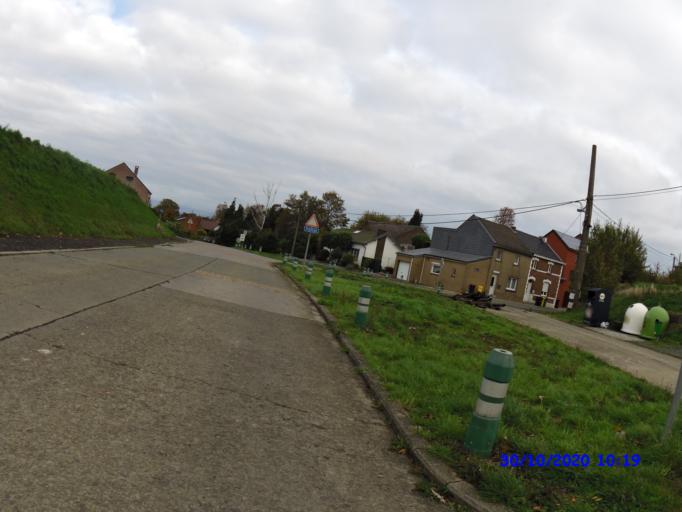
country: BE
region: Wallonia
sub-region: Province de Liege
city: Berloz
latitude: 50.7149
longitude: 5.2152
